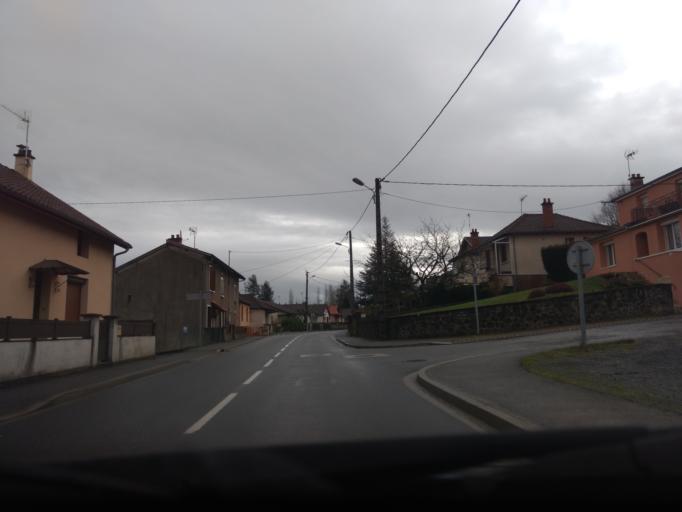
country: FR
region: Midi-Pyrenees
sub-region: Departement de l'Aveyron
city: Firmi
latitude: 44.5338
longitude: 2.3202
